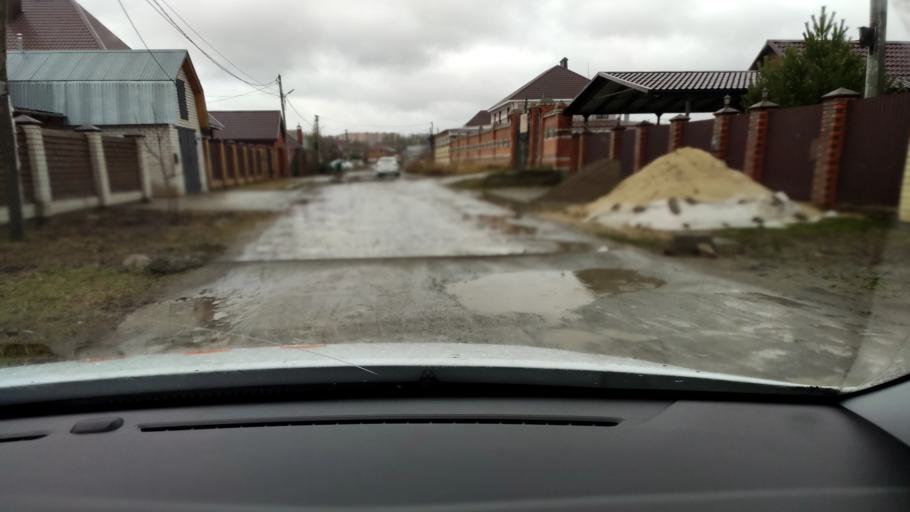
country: RU
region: Tatarstan
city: Stolbishchi
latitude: 55.7460
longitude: 49.2705
